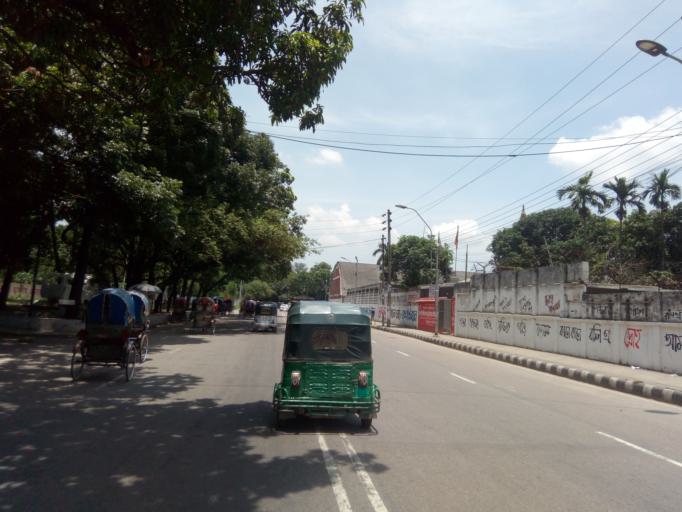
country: BD
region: Dhaka
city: Azimpur
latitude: 23.7308
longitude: 90.3954
